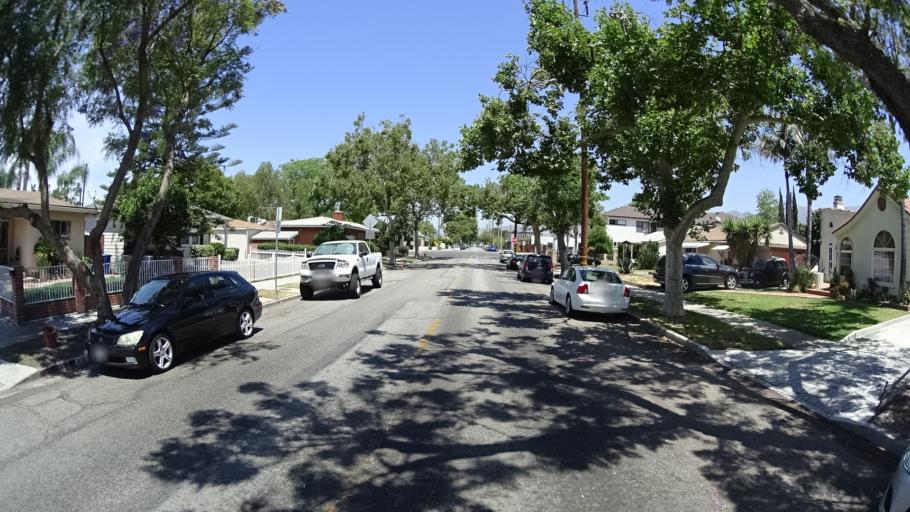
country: US
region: California
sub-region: Los Angeles County
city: Burbank
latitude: 34.1788
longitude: -118.3239
